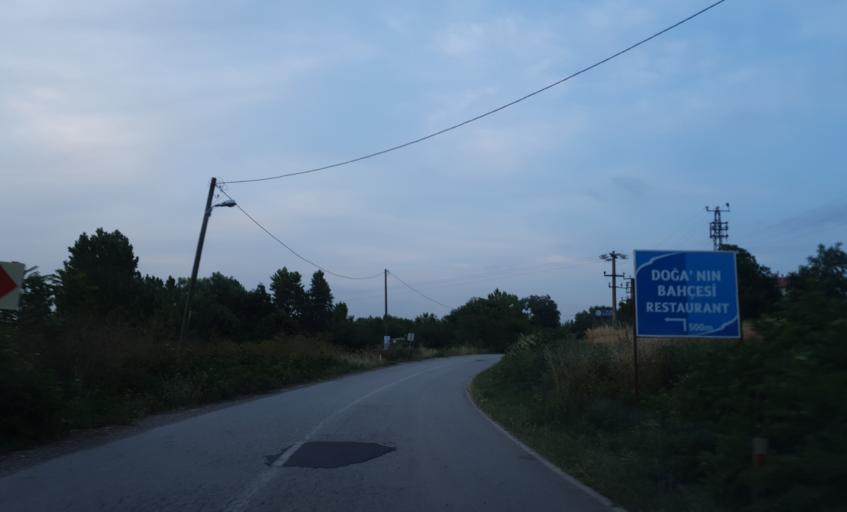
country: TR
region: Tekirdag
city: Beyazkoy
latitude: 41.3802
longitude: 27.6149
